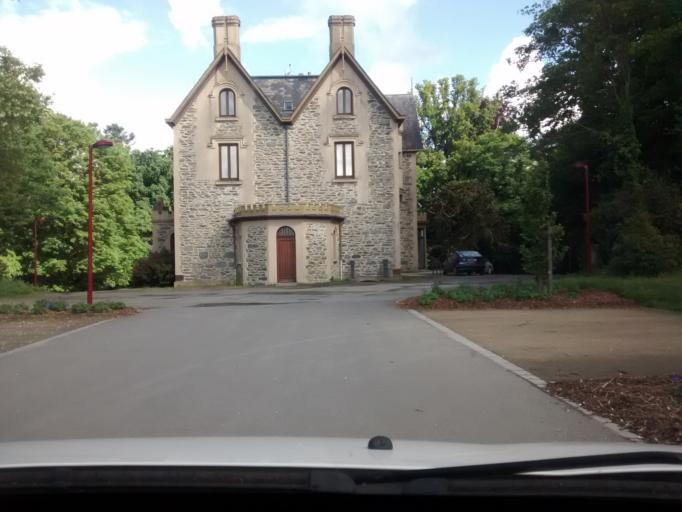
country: FR
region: Brittany
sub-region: Departement d'Ille-et-Vilaine
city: Cesson-Sevigne
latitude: 48.1089
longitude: -1.5998
